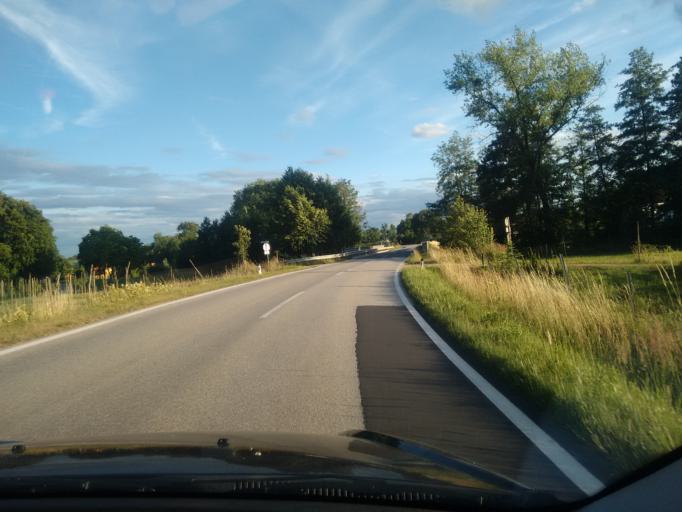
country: AT
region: Upper Austria
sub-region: Politischer Bezirk Urfahr-Umgebung
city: Feldkirchen an der Donau
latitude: 48.3634
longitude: 14.0683
